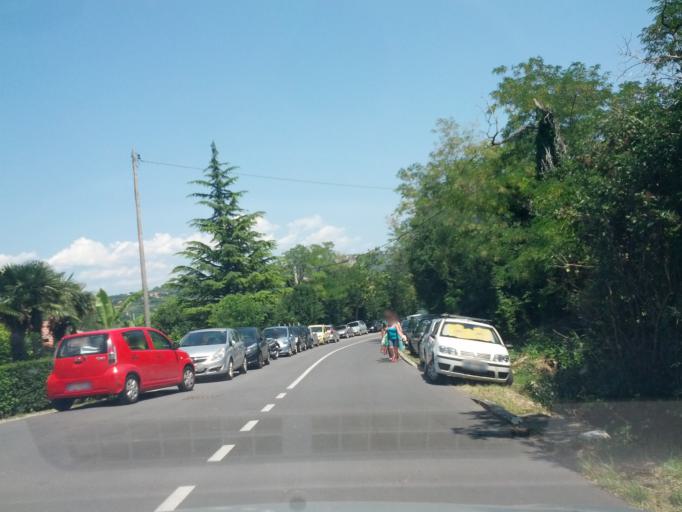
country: SI
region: Koper-Capodistria
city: Ankaran
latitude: 45.5912
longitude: 13.7140
